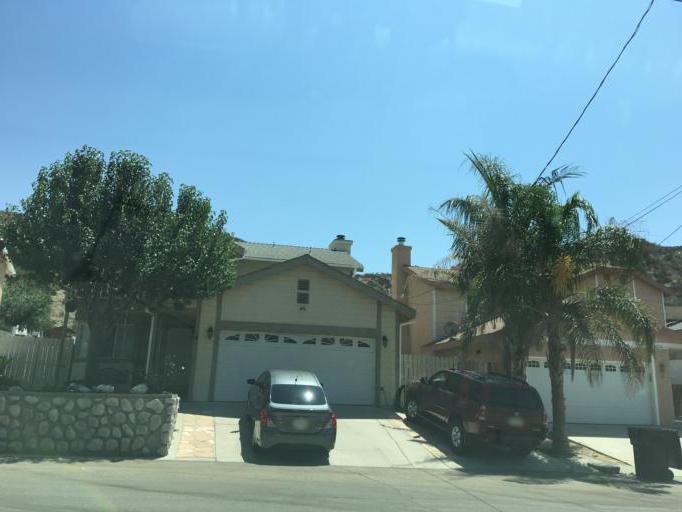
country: US
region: California
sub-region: Los Angeles County
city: Val Verde
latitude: 34.4422
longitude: -118.6558
